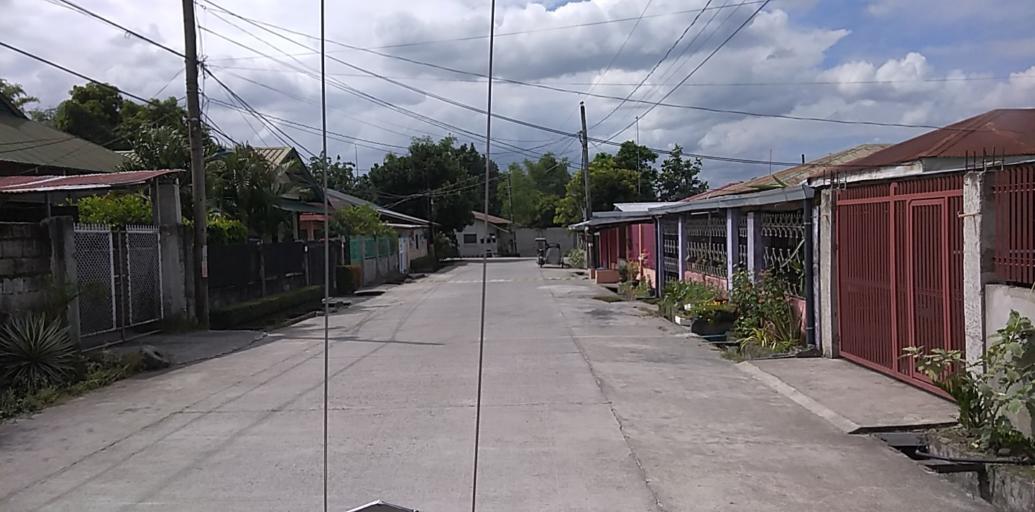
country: PH
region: Central Luzon
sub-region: Province of Pampanga
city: Porac
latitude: 15.0649
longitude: 120.5352
